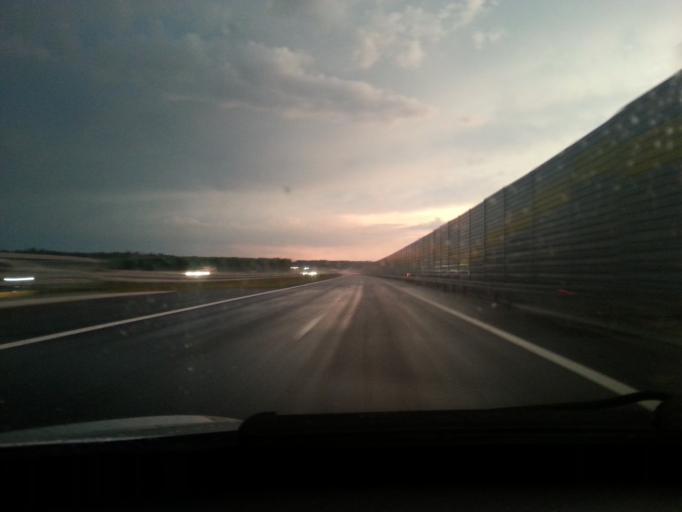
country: PL
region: Lodz Voivodeship
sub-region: Powiat pabianicki
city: Dobron
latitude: 51.5903
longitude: 19.2122
